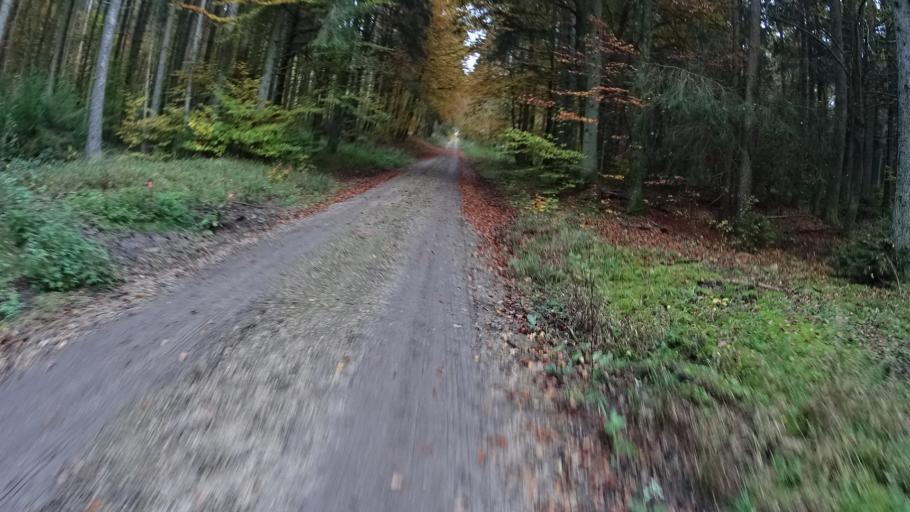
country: DE
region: Bavaria
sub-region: Upper Bavaria
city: Hitzhofen
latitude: 48.8655
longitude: 11.2836
